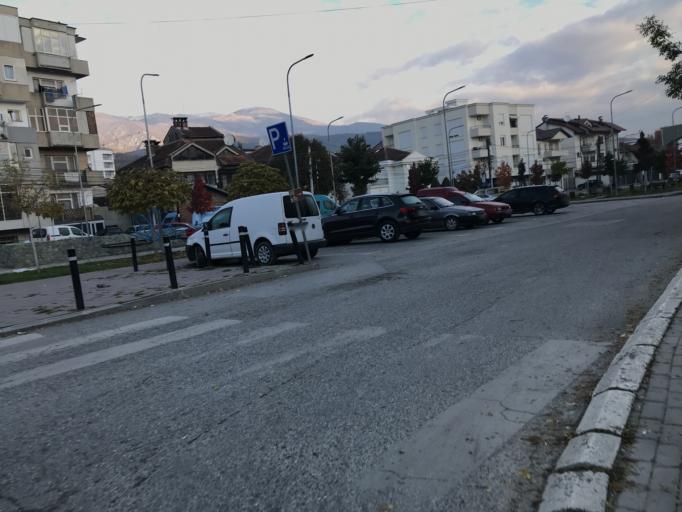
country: XK
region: Pec
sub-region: Komuna e Pejes
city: Peje
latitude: 42.6616
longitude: 20.2993
